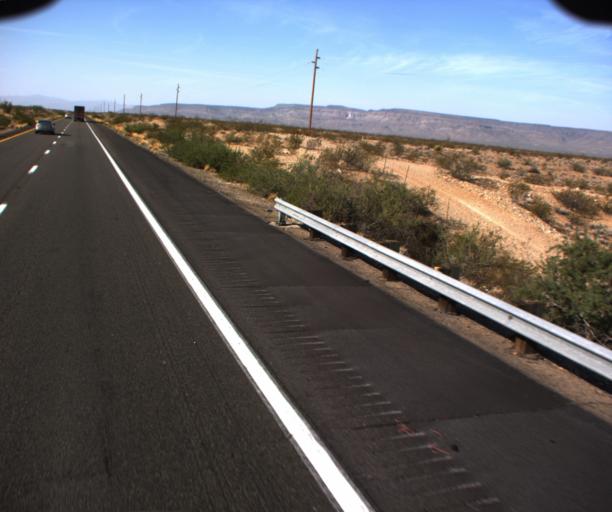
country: US
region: Arizona
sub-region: Mohave County
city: Kingman
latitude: 34.9818
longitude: -114.1405
